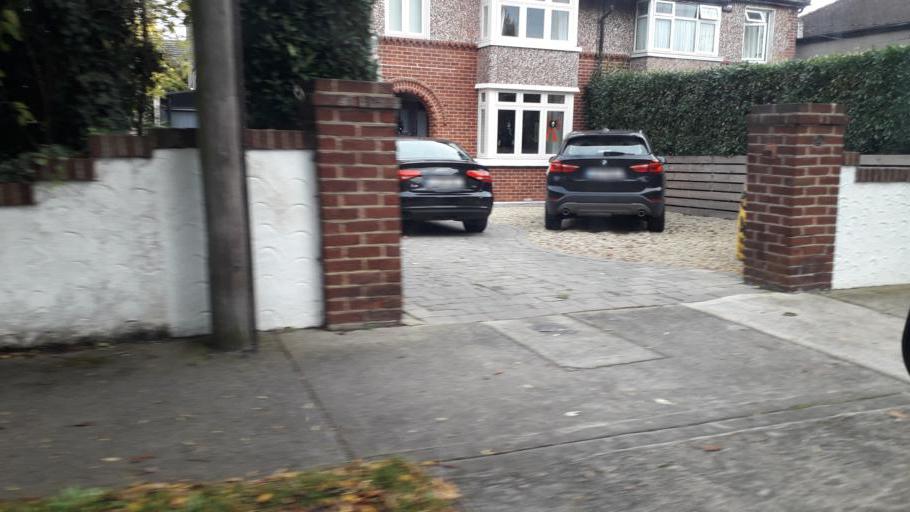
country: IE
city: Milltown
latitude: 53.3079
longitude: -6.2394
